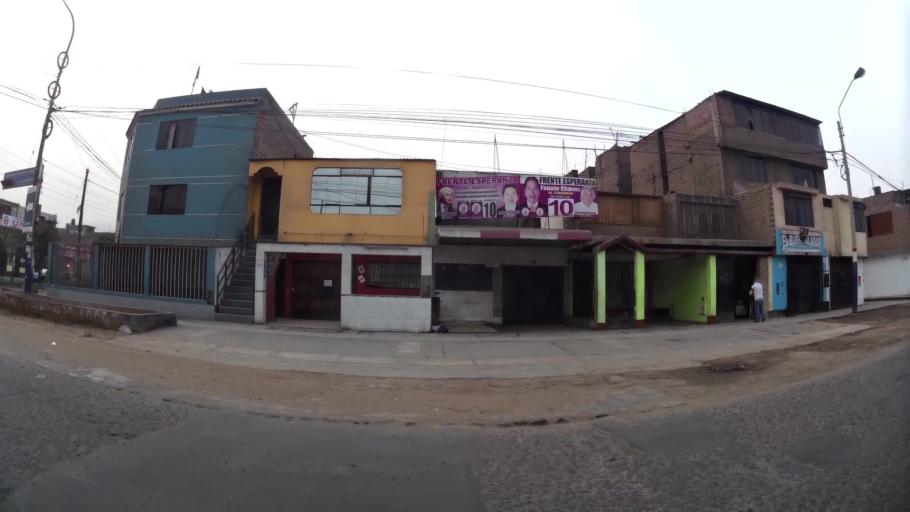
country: PE
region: Lima
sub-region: Lima
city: Independencia
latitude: -11.9960
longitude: -77.0049
